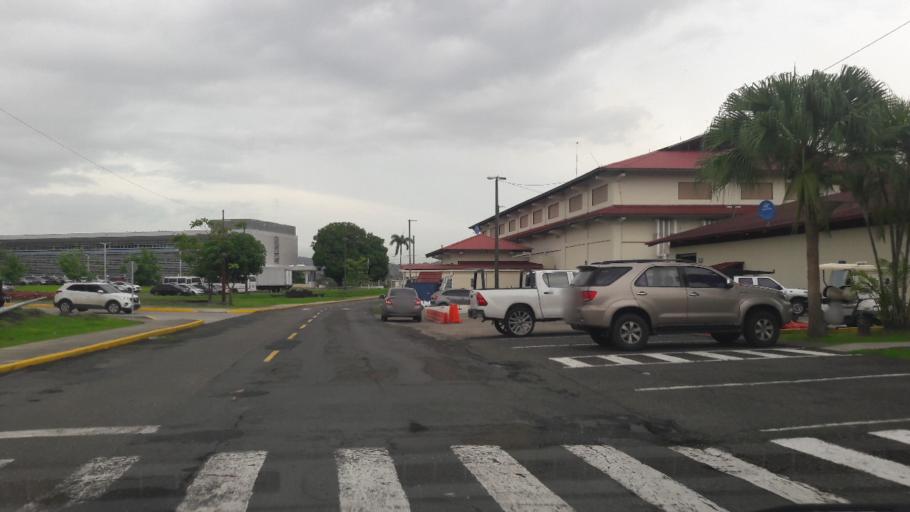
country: PA
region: Panama
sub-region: Distrito de Panama
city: Paraiso
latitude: 9.0028
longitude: -79.5849
